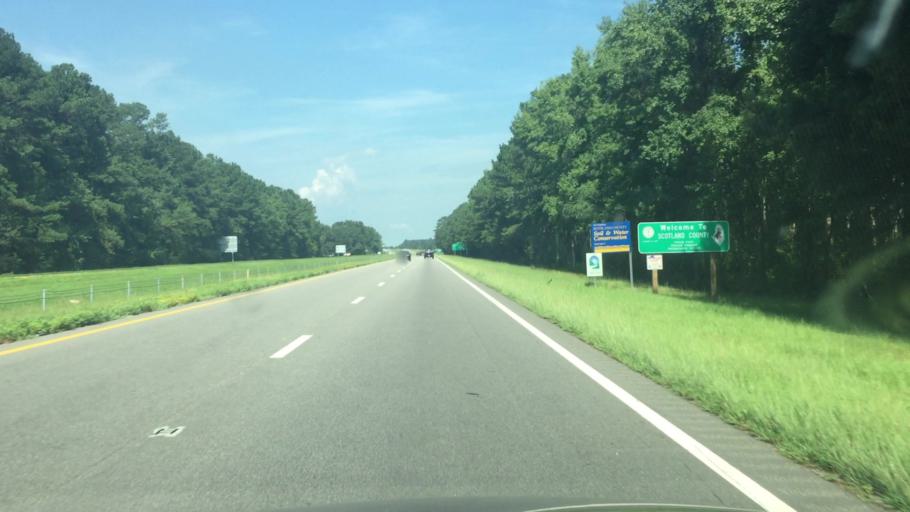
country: US
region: North Carolina
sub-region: Robeson County
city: Maxton
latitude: 34.7527
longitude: -79.3534
